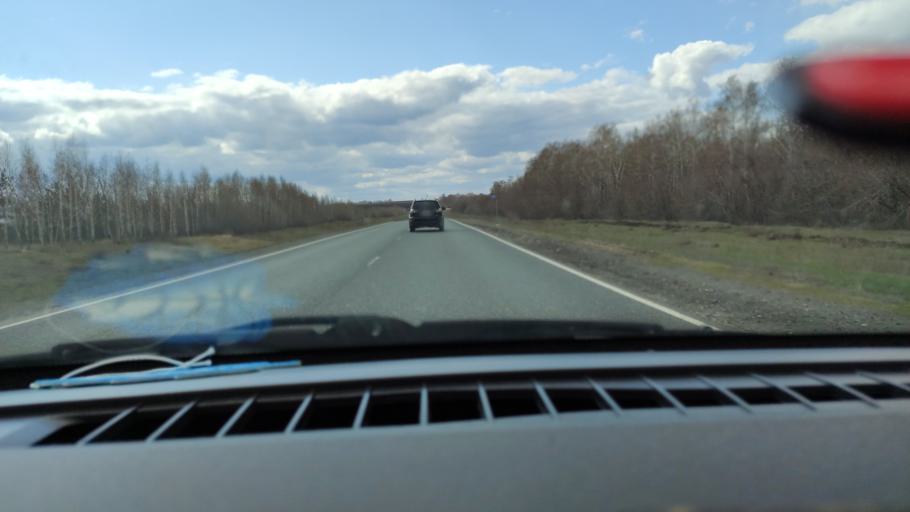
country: RU
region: Saratov
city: Balakovo
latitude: 52.1385
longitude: 47.7986
